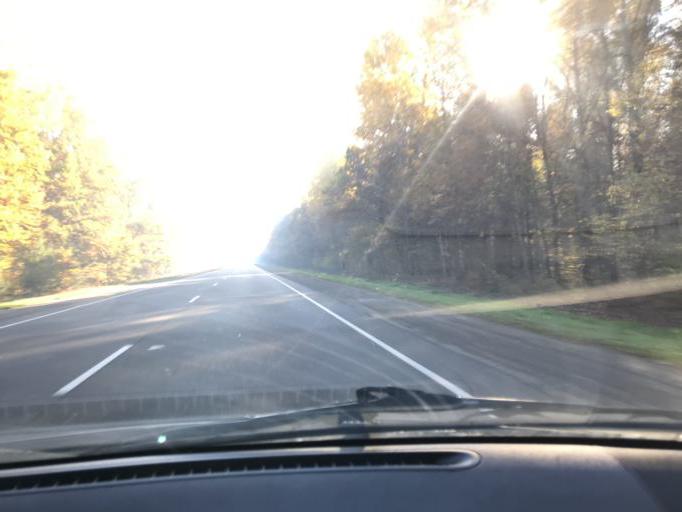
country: BY
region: Brest
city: Horad Luninyets
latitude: 52.2927
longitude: 26.7635
